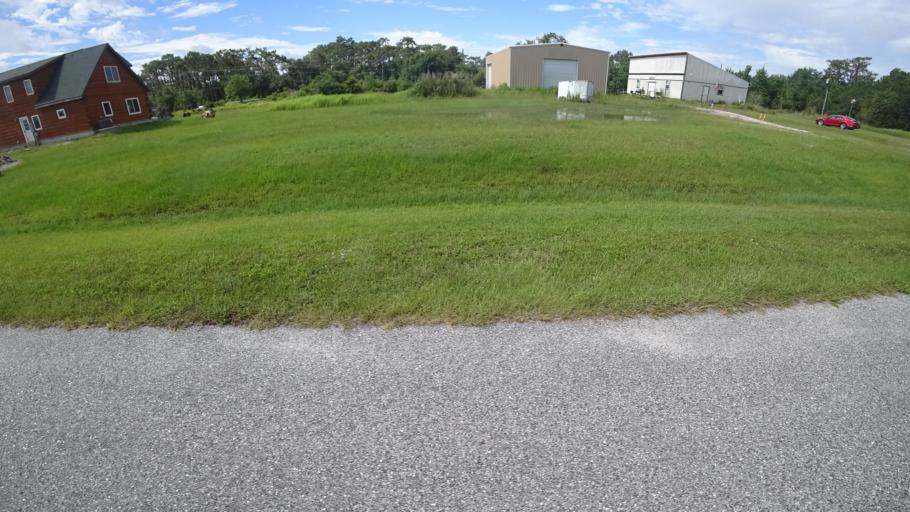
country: US
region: Florida
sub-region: Sarasota County
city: Lake Sarasota
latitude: 27.3882
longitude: -82.2771
